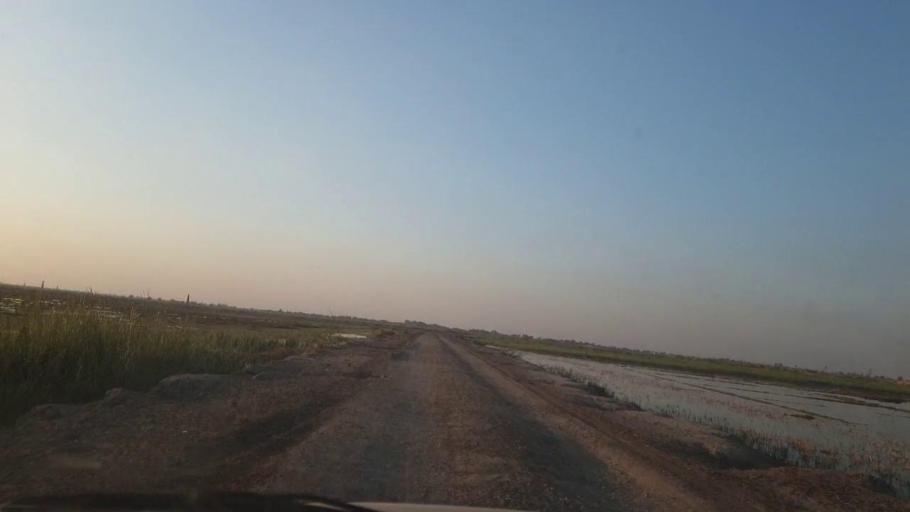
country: PK
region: Sindh
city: Mirpur Khas
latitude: 25.4550
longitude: 69.0738
